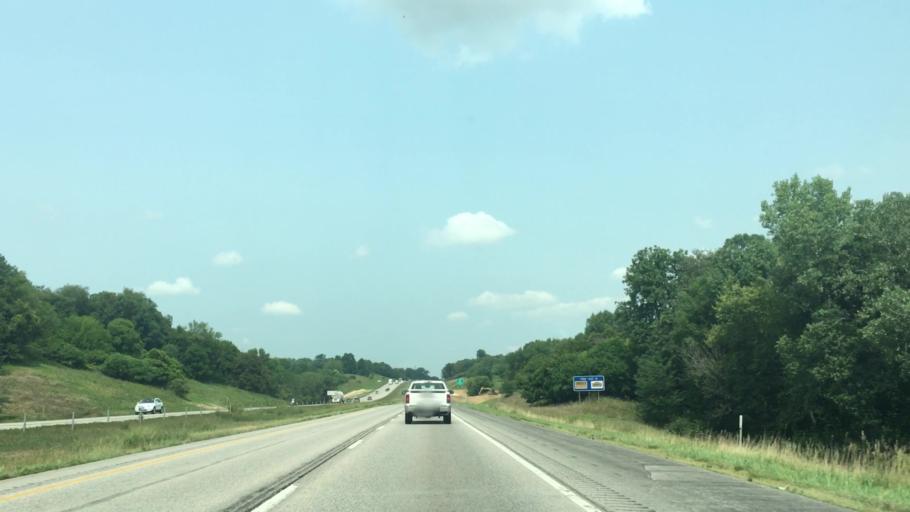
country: US
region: Iowa
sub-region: Linn County
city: Ely
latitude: 41.8250
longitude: -91.6576
